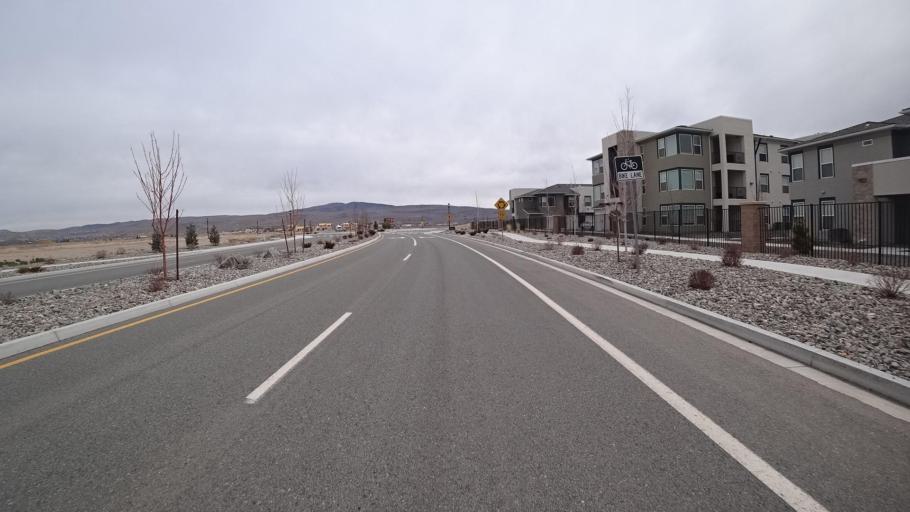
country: US
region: Nevada
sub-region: Washoe County
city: Spanish Springs
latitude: 39.6149
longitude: -119.7119
